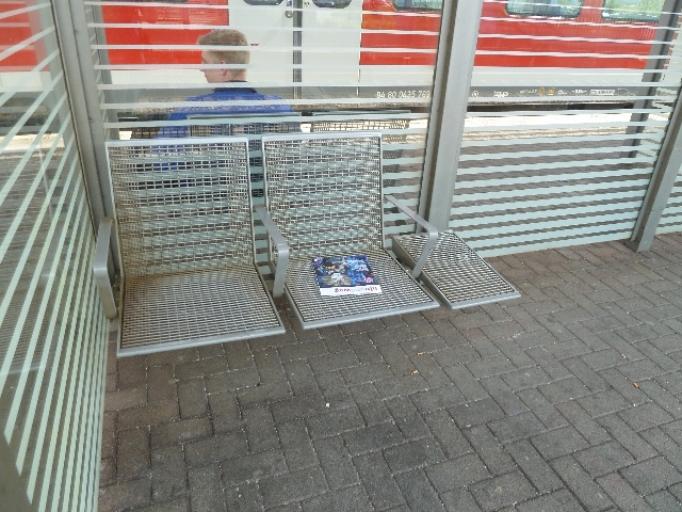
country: DE
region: Baden-Wuerttemberg
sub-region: Karlsruhe Region
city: Waghausel
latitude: 49.2483
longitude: 8.5084
